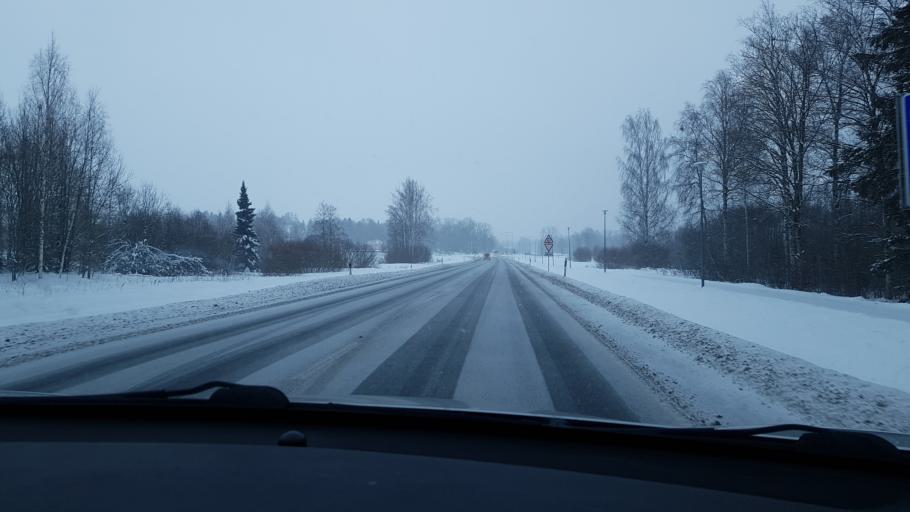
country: EE
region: Jaervamaa
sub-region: Tueri vald
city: Tueri
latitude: 58.8444
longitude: 25.4771
